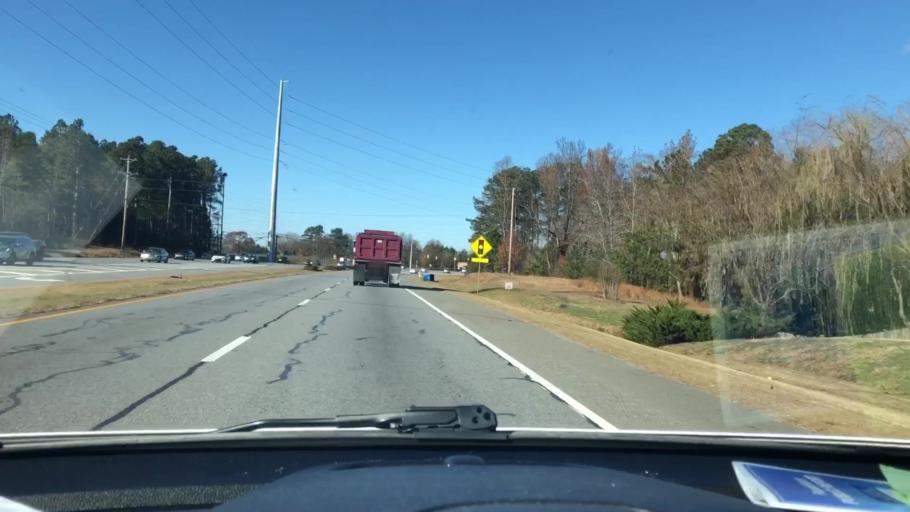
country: US
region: Georgia
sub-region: Forsyth County
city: Cumming
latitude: 34.1326
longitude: -84.1725
